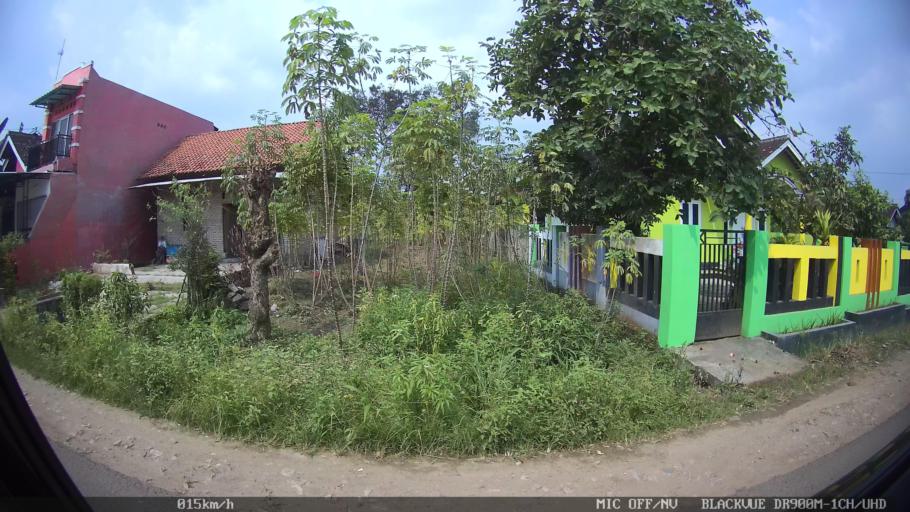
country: ID
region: Lampung
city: Gadingrejo
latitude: -5.3615
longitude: 105.0464
